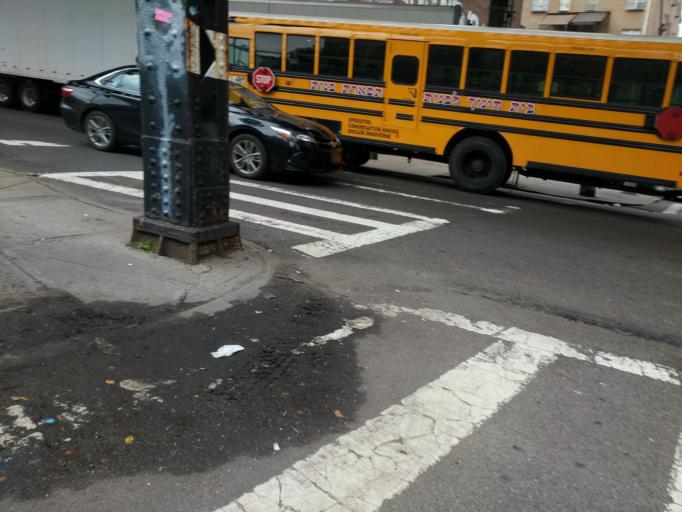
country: US
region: New York
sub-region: Queens County
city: Long Island City
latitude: 40.7032
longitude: -73.9461
